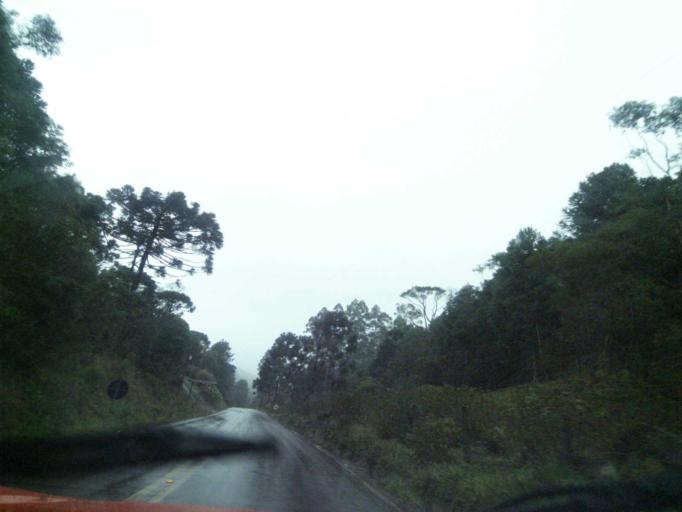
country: BR
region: Santa Catarina
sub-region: Anitapolis
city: Anitapolis
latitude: -27.8013
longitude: -49.0459
